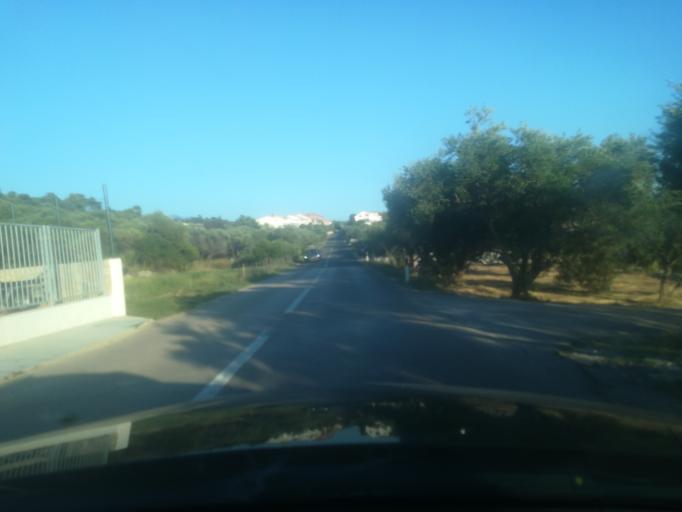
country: HR
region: Primorsko-Goranska
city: Banjol
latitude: 44.7337
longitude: 14.8090
